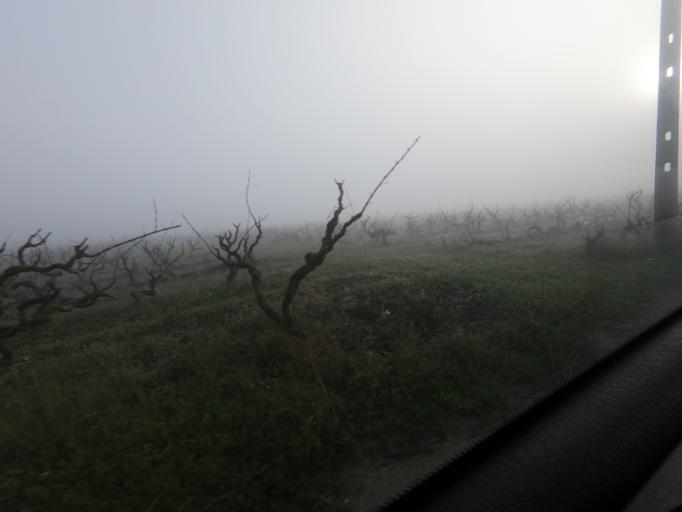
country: PT
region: Setubal
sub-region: Palmela
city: Palmela
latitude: 38.6003
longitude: -8.8465
